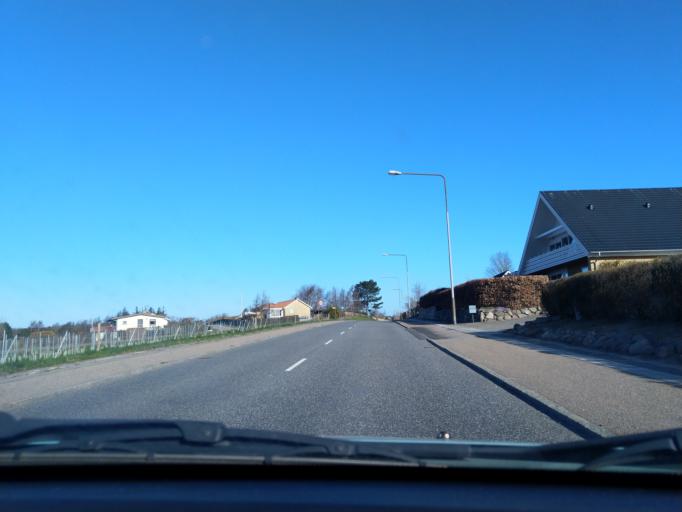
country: DK
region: Zealand
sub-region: Kalundborg Kommune
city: Kalundborg
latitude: 55.7076
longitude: 11.0219
